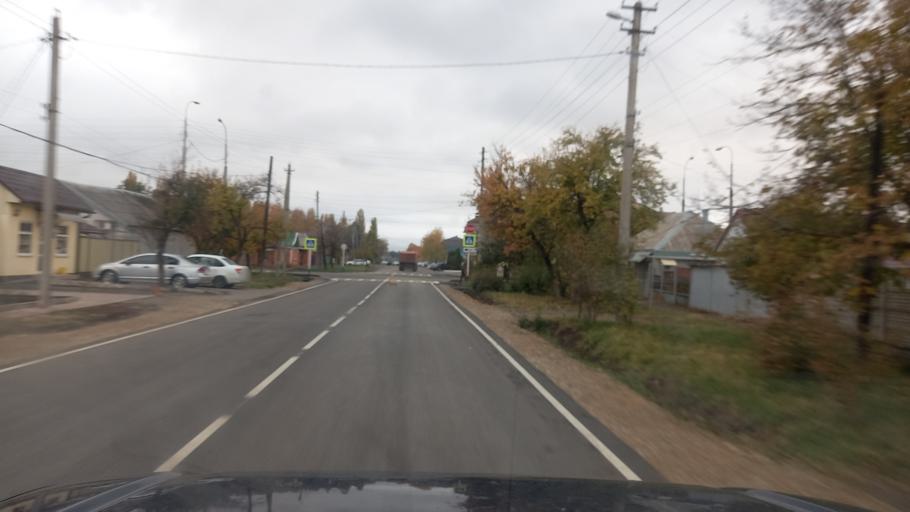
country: RU
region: Adygeya
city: Maykop
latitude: 44.6191
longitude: 40.1247
